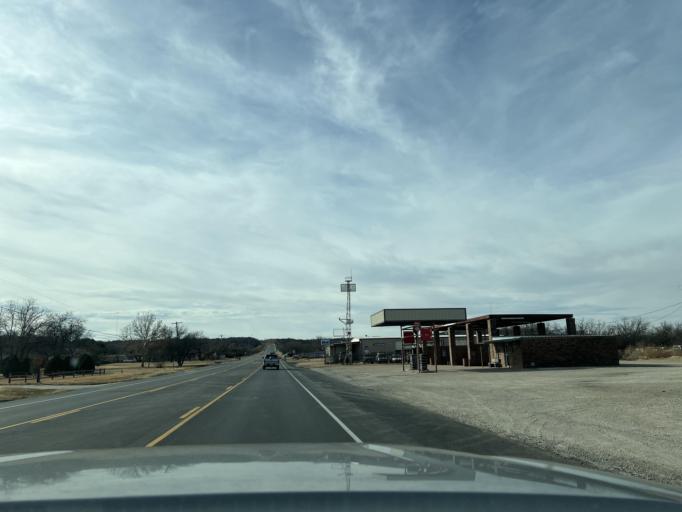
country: US
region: Texas
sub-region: Shackelford County
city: Albany
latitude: 32.7180
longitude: -99.3023
